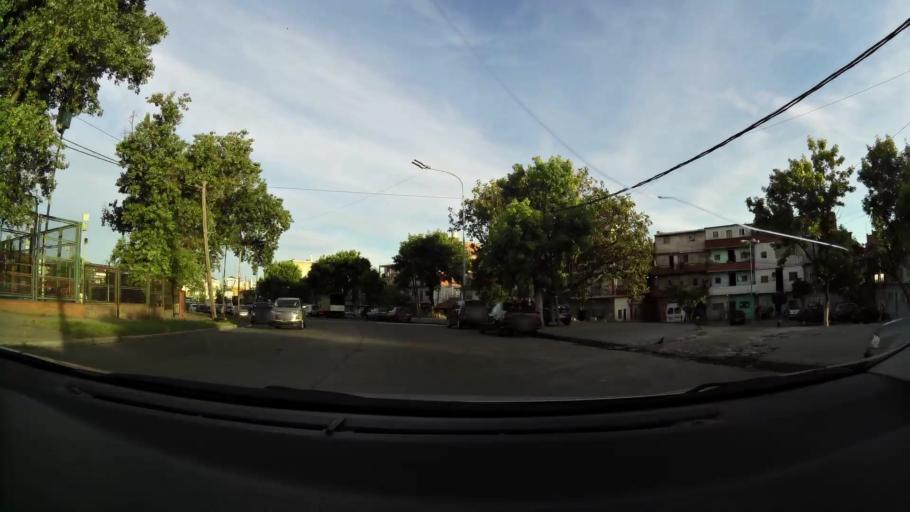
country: AR
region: Buenos Aires F.D.
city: Villa Lugano
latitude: -34.6437
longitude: -58.4431
